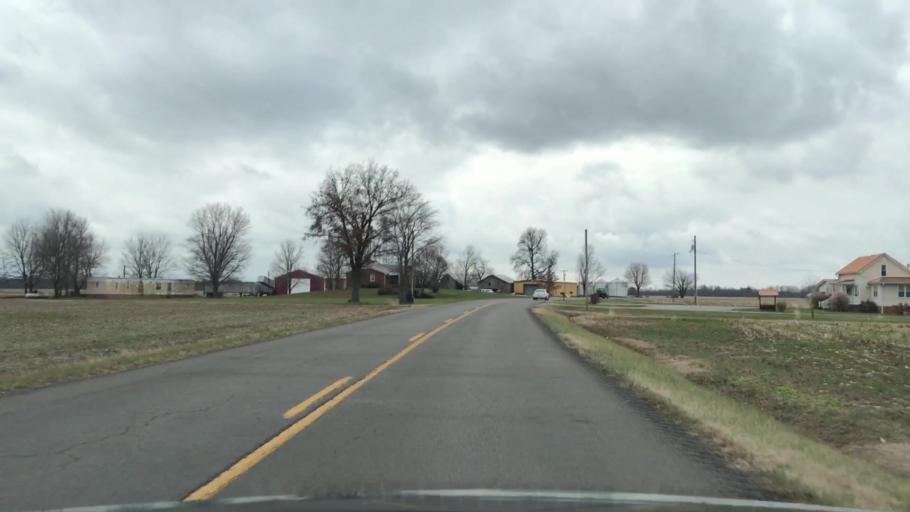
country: US
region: Kentucky
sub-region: McLean County
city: Calhoun
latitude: 37.5273
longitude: -87.3308
